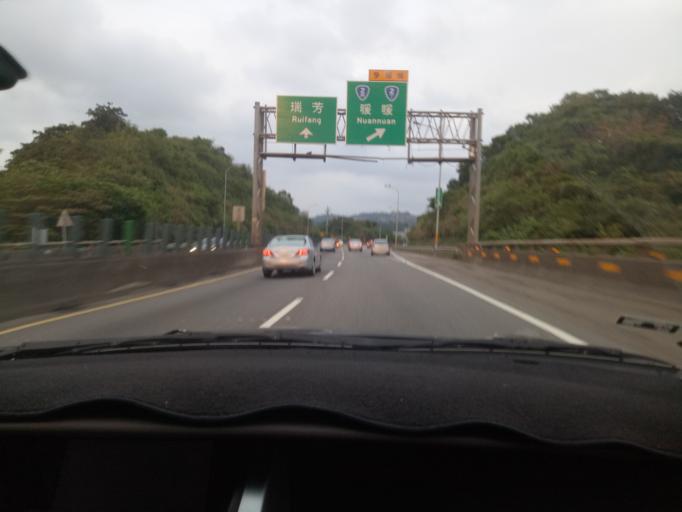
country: TW
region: Taiwan
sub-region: Keelung
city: Keelung
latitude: 25.1046
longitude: 121.7296
